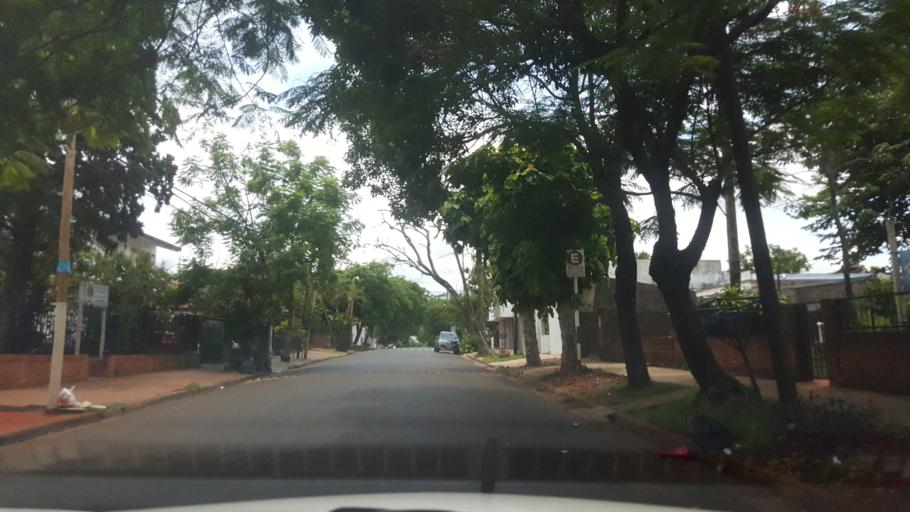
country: AR
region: Misiones
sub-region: Departamento de Capital
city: Posadas
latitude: -27.3873
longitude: -55.8947
